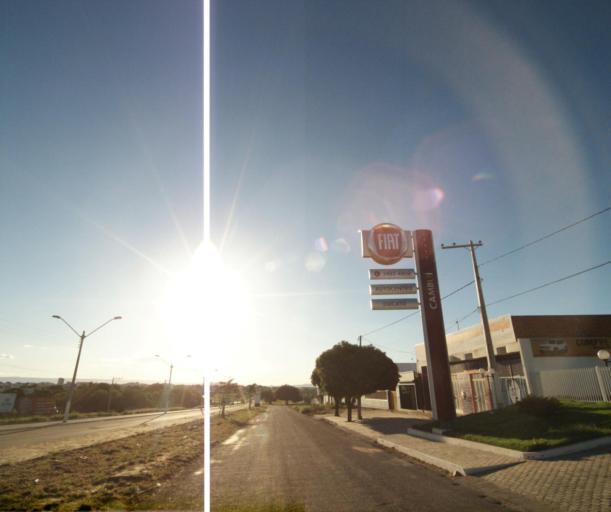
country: BR
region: Bahia
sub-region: Guanambi
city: Guanambi
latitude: -14.2091
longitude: -42.7700
